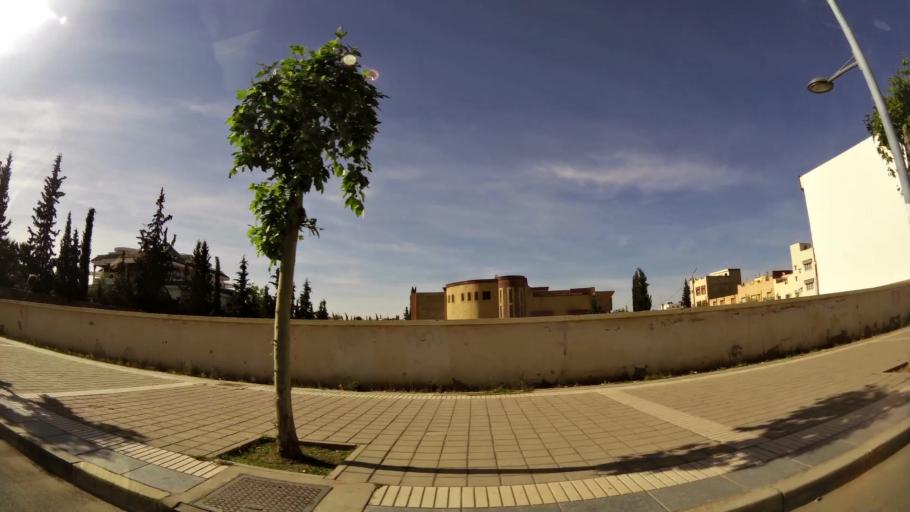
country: MA
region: Oriental
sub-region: Oujda-Angad
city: Oujda
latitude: 34.6638
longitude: -1.9002
